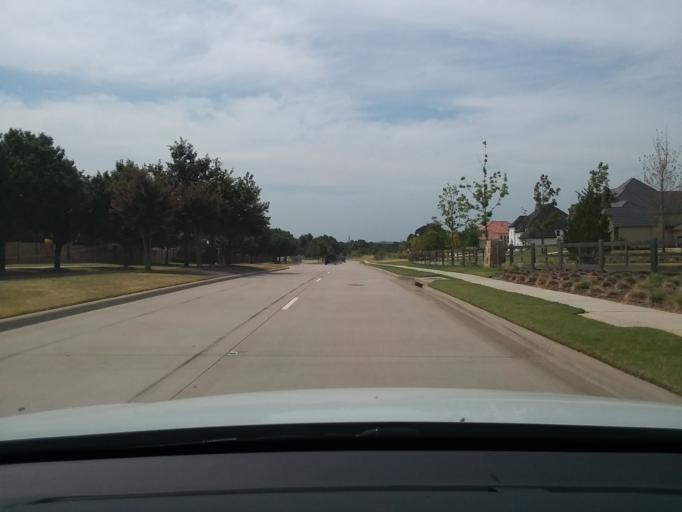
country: US
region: Texas
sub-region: Denton County
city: Flower Mound
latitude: 33.0344
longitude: -97.1052
